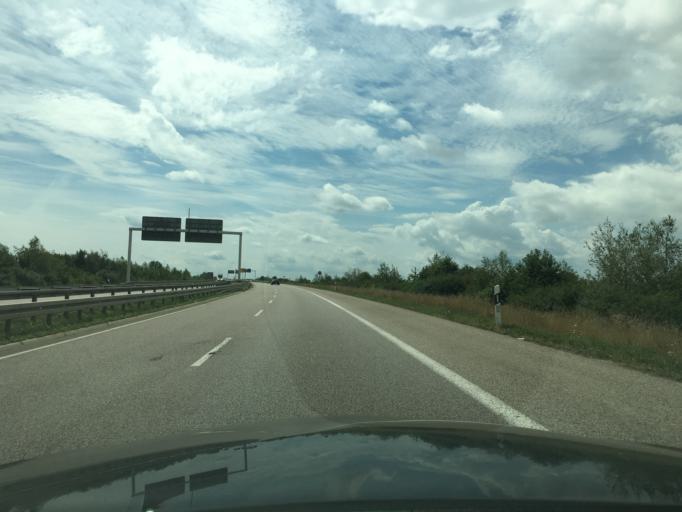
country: DE
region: Saxony-Anhalt
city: Brehna
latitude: 51.5628
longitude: 12.1945
